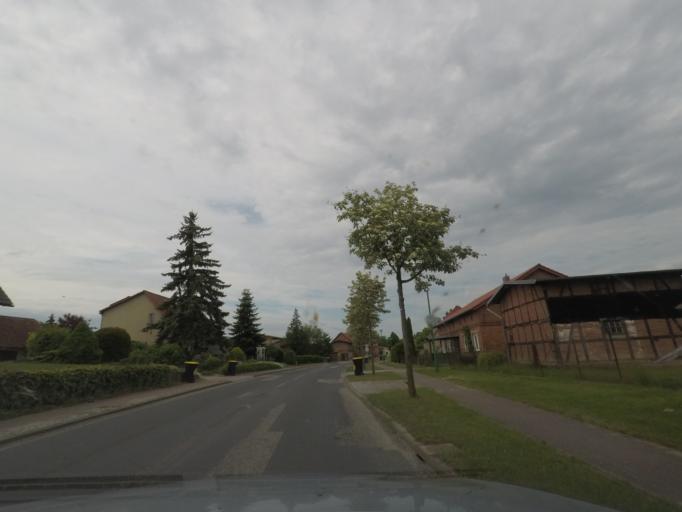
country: DE
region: Brandenburg
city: Schenkenberg
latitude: 53.3476
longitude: 13.9534
